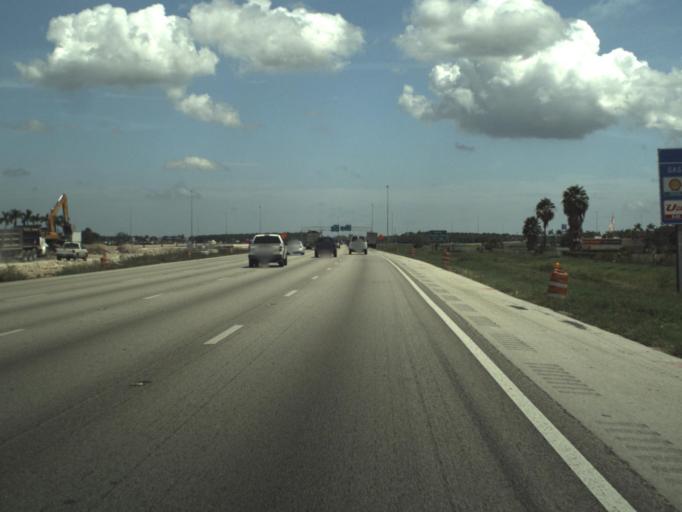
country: US
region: Florida
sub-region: Broward County
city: Southwest Ranches
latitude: 26.0727
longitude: -80.3592
